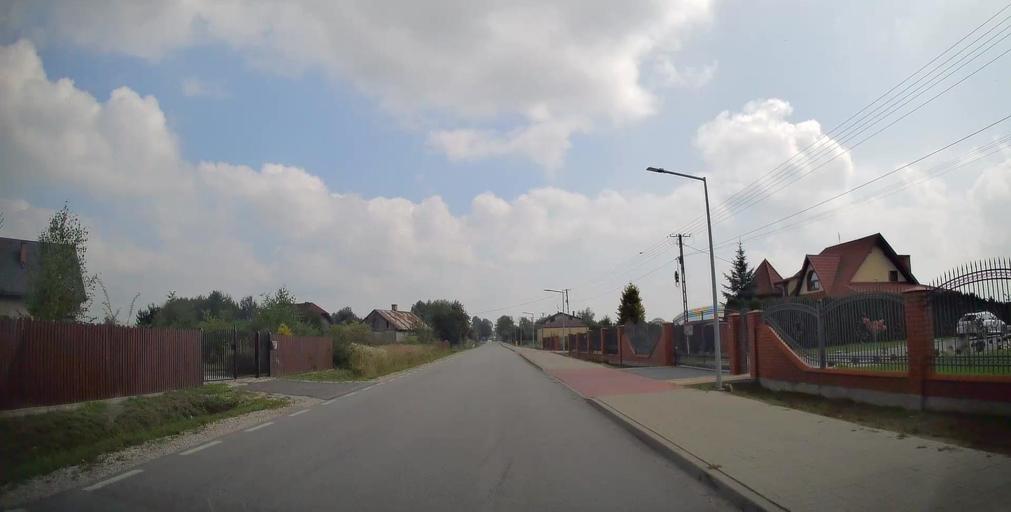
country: PL
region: Masovian Voivodeship
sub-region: Powiat bialobrzeski
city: Sucha
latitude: 51.6103
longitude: 20.9740
